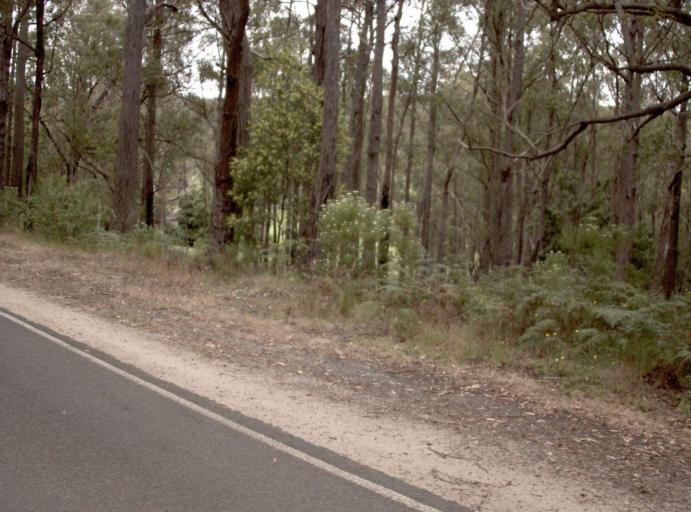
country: AU
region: Victoria
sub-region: Latrobe
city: Traralgon
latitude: -38.4940
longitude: 146.6434
